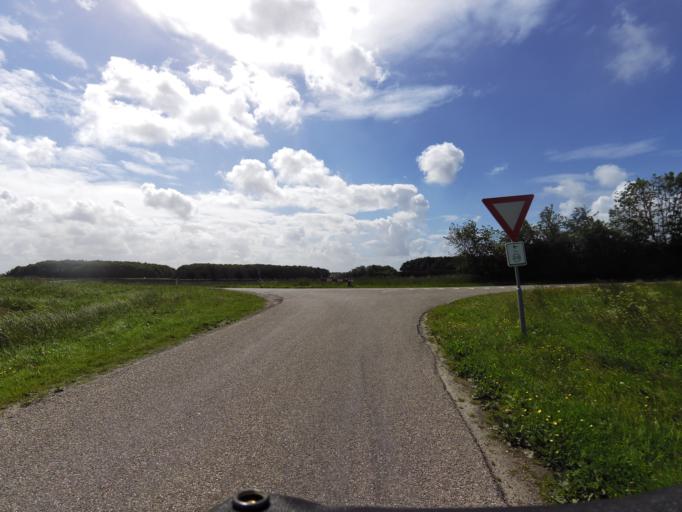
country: NL
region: Zeeland
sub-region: Schouwen-Duiveland
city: Bruinisse
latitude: 51.6843
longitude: 4.0049
